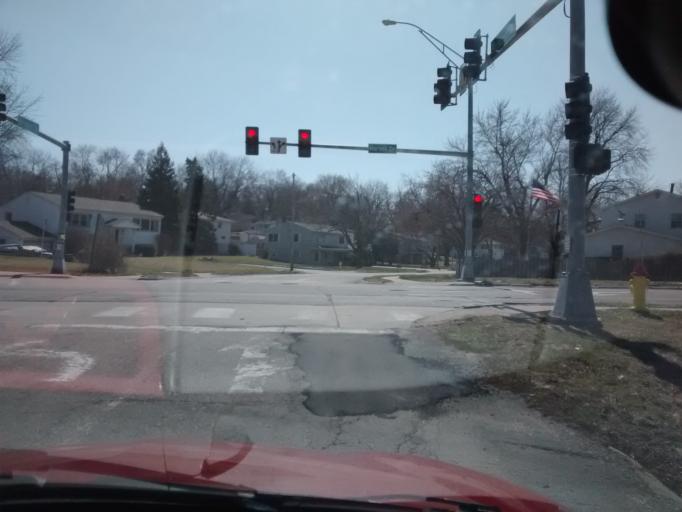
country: US
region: Nebraska
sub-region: Sarpy County
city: Bellevue
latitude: 41.1515
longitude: -95.9130
